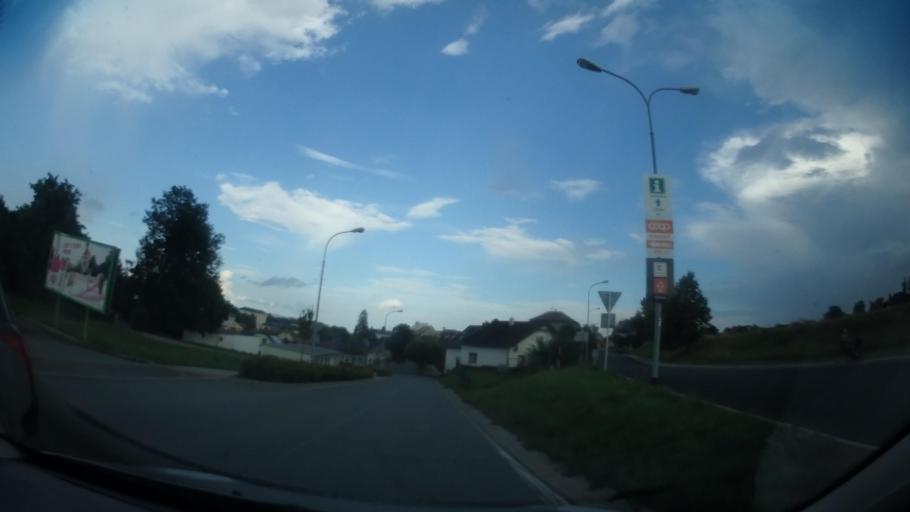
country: CZ
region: Olomoucky
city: Zabreh
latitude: 49.8852
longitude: 16.8604
